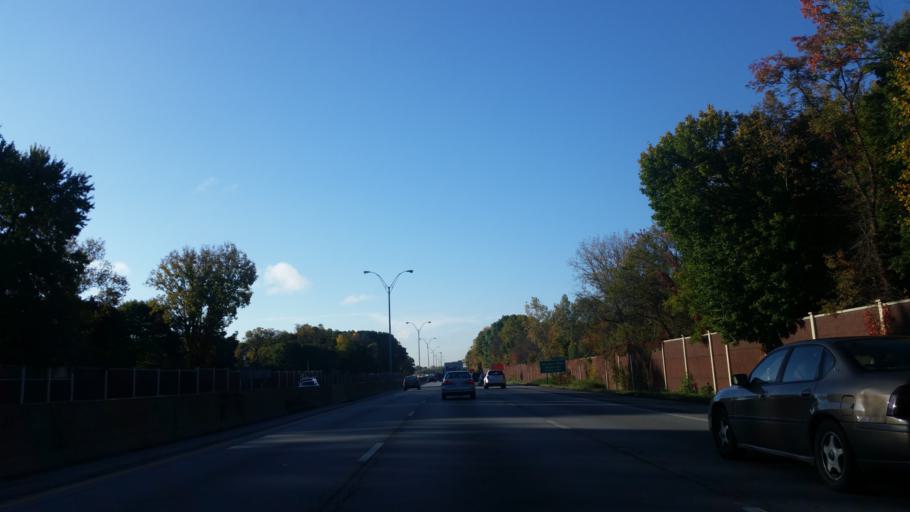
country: US
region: Ohio
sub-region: Summit County
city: Akron
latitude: 41.0753
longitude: -81.5741
